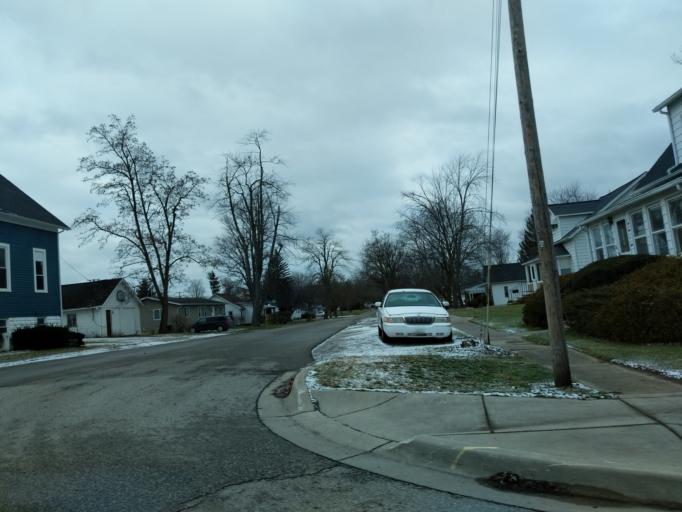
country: US
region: Michigan
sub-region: Sanilac County
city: Marlette
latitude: 43.3270
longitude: -83.0812
